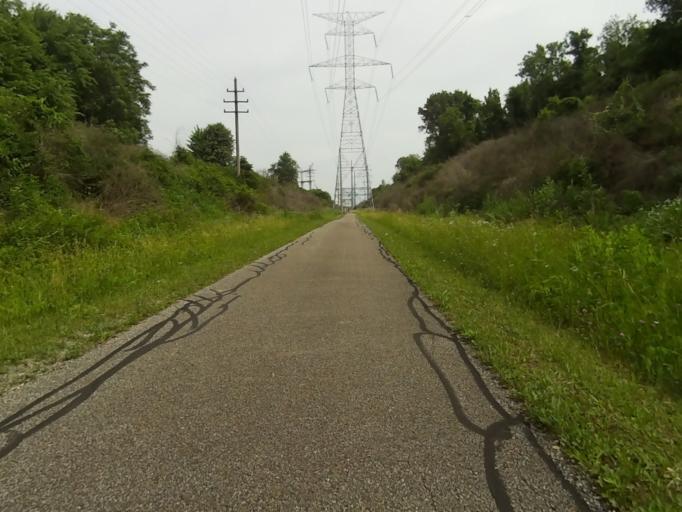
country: US
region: Ohio
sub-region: Cuyahoga County
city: Walton Hills
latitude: 41.3250
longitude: -81.5693
